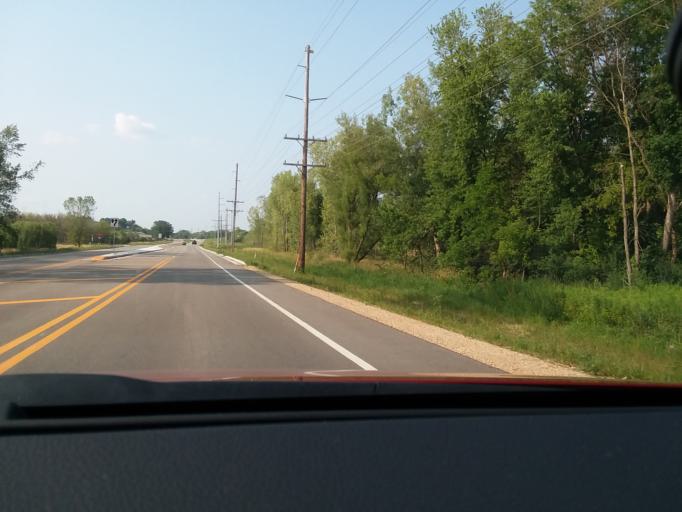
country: US
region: Wisconsin
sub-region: Dane County
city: Sun Prairie
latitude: 43.1503
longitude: -89.2656
